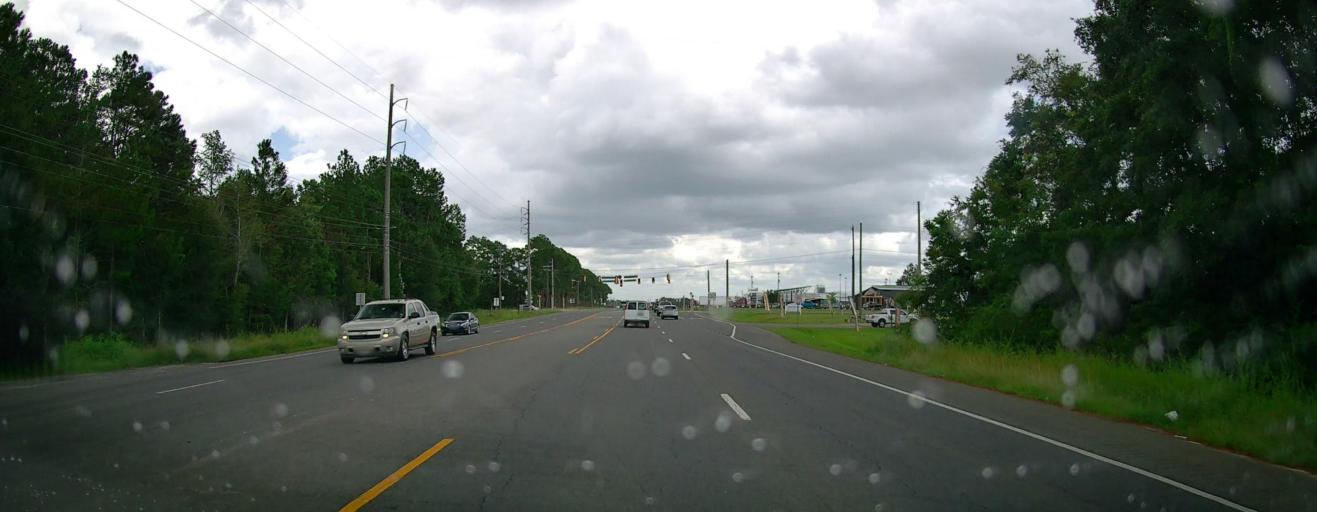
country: US
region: Georgia
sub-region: Coffee County
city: Douglas
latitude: 31.4881
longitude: -82.8615
